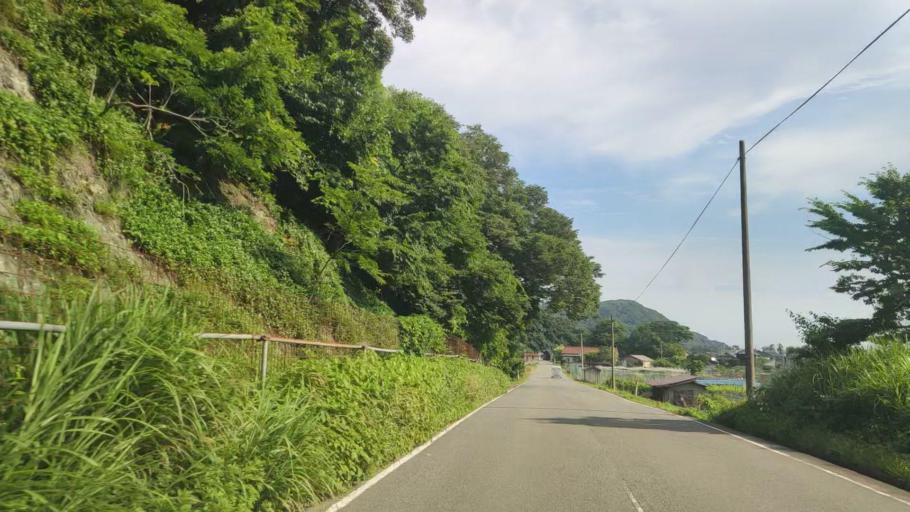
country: JP
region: Hyogo
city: Toyooka
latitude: 35.6359
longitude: 134.8366
